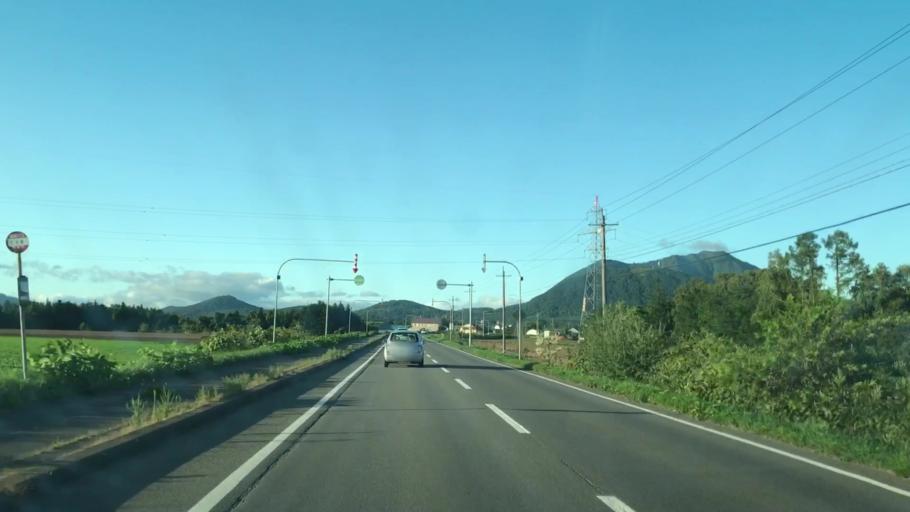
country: JP
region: Hokkaido
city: Niseko Town
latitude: 42.7194
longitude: 140.8601
